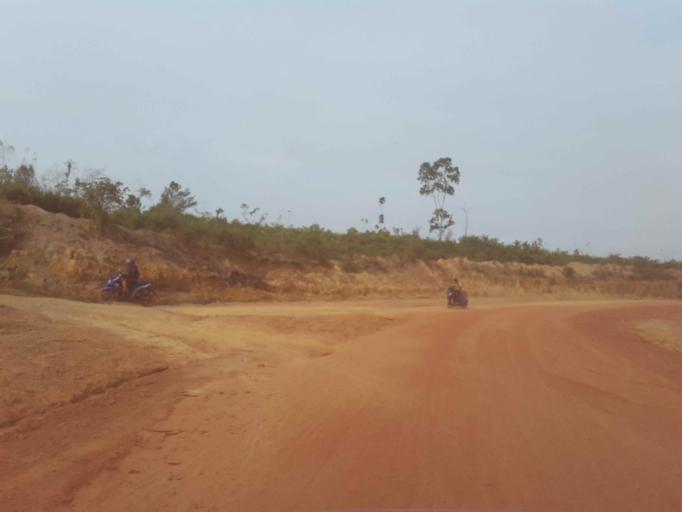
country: MY
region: Sarawak
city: Simanggang
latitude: 0.8853
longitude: 111.0302
